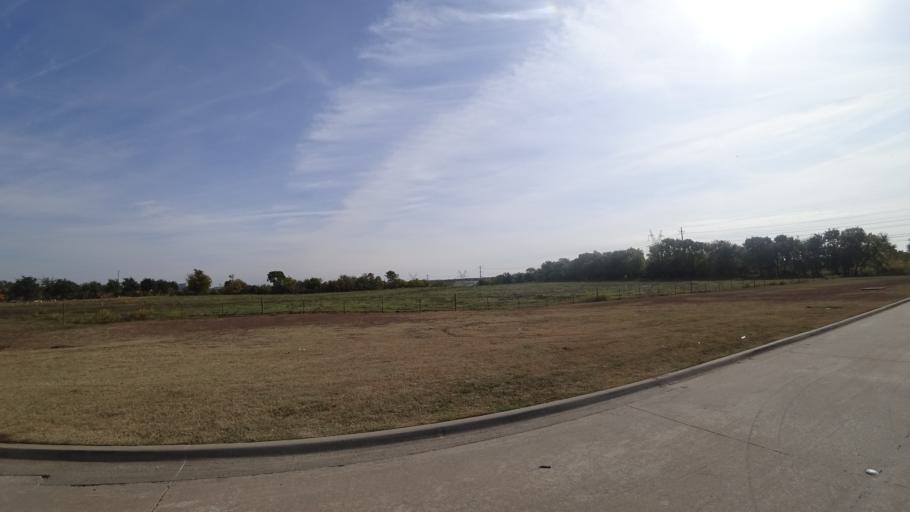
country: US
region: Texas
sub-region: Denton County
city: The Colony
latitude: 33.0625
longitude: -96.8714
